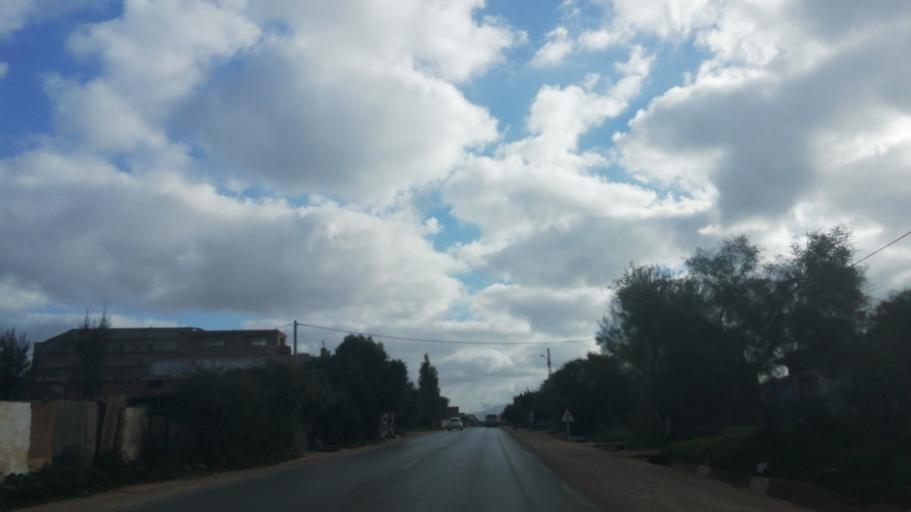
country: DZ
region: Relizane
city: Mazouna
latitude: 36.2586
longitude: 0.5988
